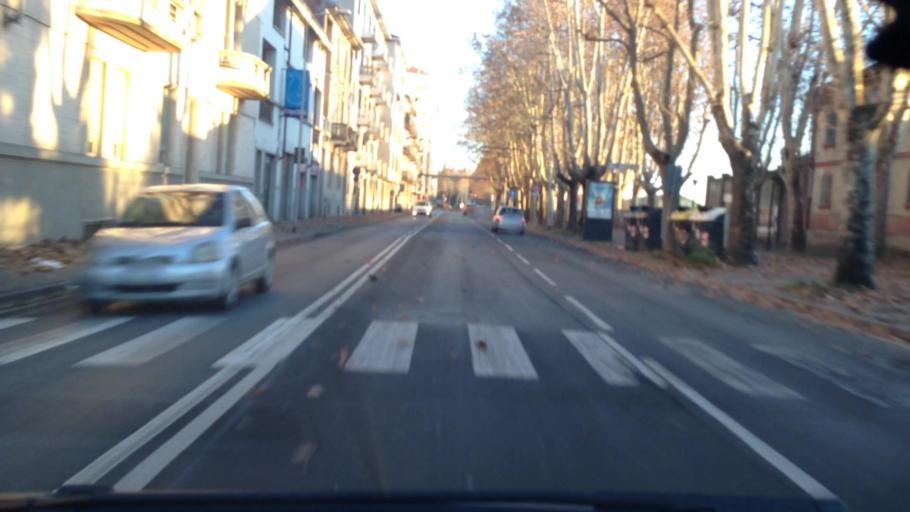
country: IT
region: Piedmont
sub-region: Provincia di Alessandria
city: Alessandria
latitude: 44.9135
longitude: 8.6033
